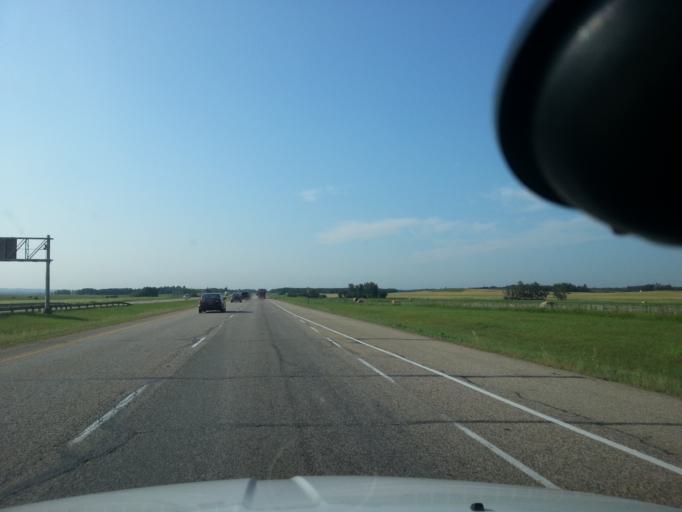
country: CA
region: Alberta
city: Millet
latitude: 52.9559
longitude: -113.6465
